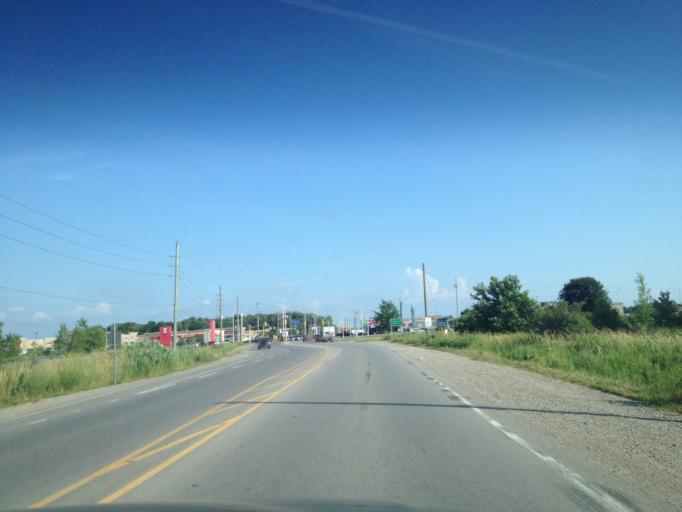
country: CA
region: Ontario
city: London
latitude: 43.0122
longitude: -81.3392
